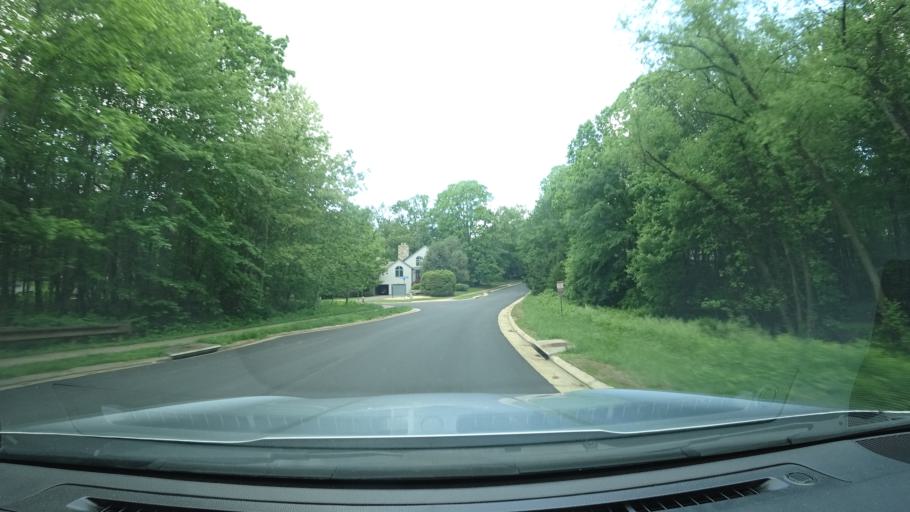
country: US
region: Virginia
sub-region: Fairfax County
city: Reston
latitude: 38.9707
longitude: -77.3472
